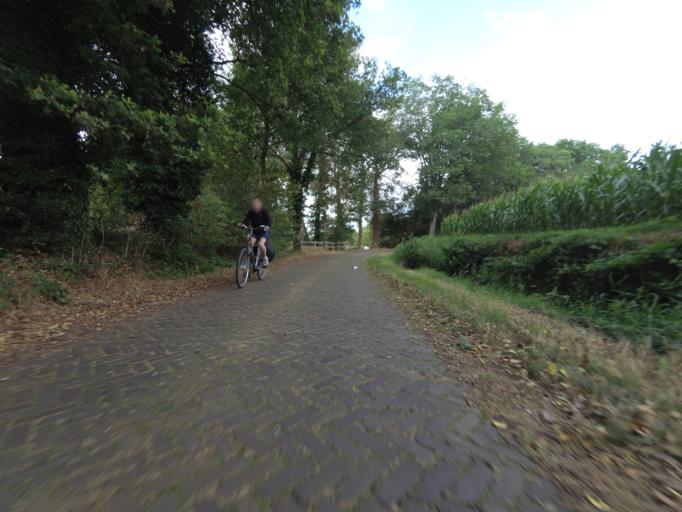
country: NL
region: Overijssel
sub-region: Gemeente Hof van Twente
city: Delden
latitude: 52.2841
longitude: 6.6671
